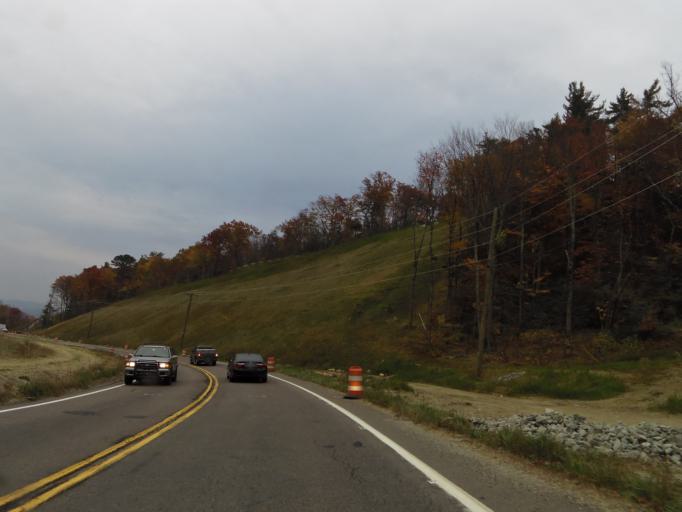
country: US
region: North Carolina
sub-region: Watauga County
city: Blowing Rock
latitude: 36.1073
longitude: -81.6543
